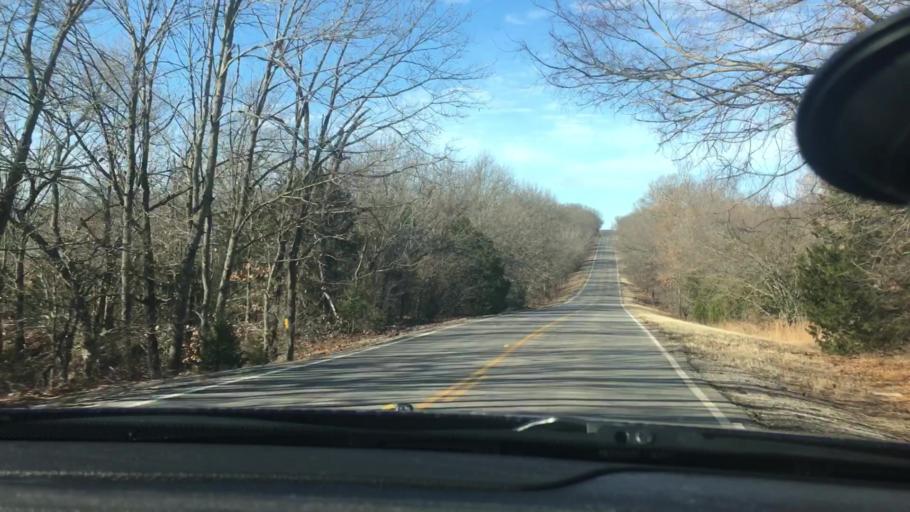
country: US
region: Oklahoma
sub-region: Seminole County
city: Konawa
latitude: 34.9856
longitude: -96.8328
